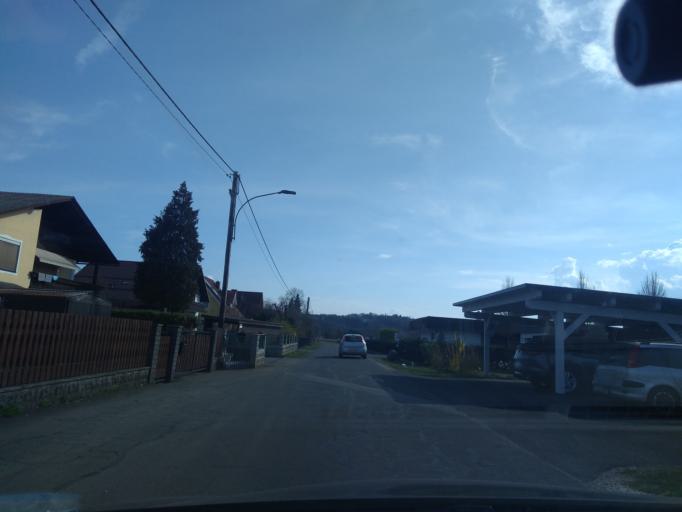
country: AT
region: Styria
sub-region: Politischer Bezirk Suedoststeiermark
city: Eichfeld
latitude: 46.7123
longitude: 15.7295
